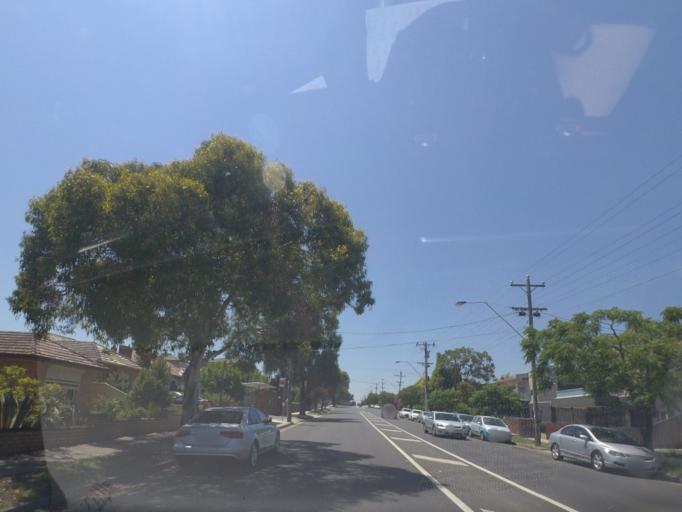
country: AU
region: Victoria
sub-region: Moreland
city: Pascoe Vale
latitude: -37.7274
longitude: 144.9391
